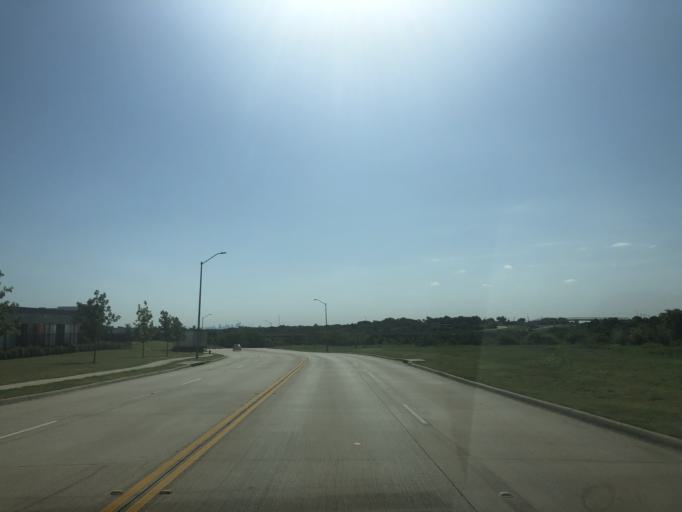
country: US
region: Texas
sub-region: Dallas County
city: Grand Prairie
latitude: 32.7507
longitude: -97.0333
